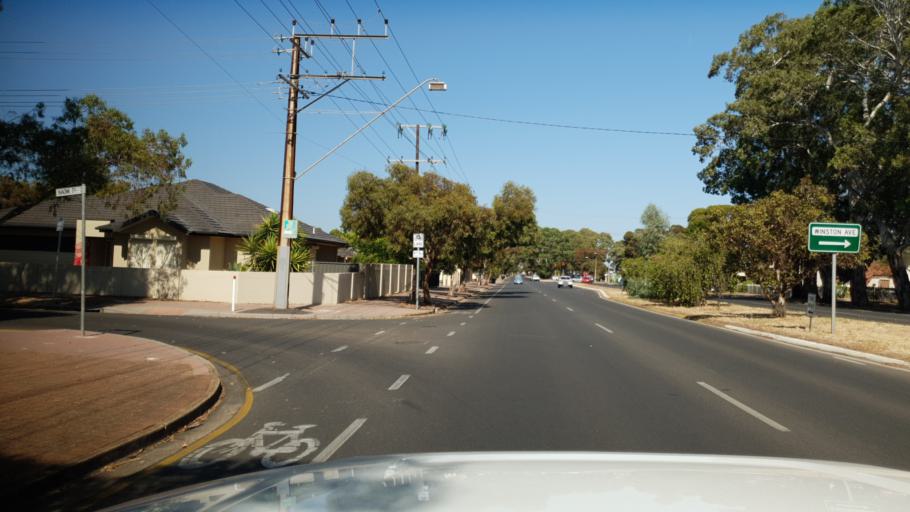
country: AU
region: South Australia
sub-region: Mitcham
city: Clapham
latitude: -34.9924
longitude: 138.5857
